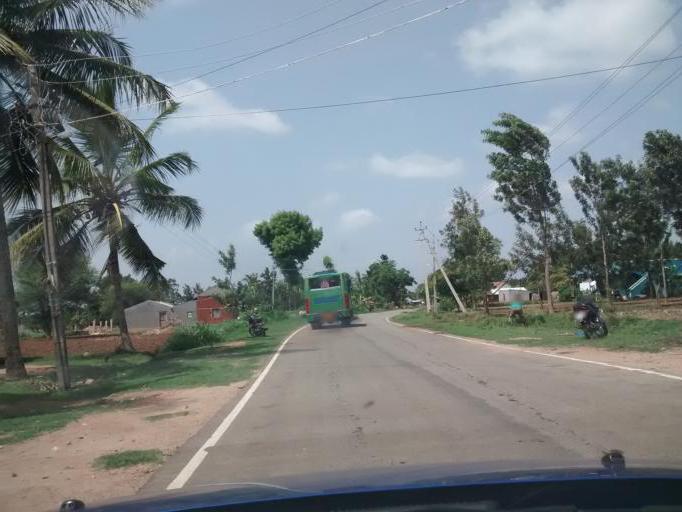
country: IN
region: Karnataka
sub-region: Hassan
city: Hole Narsipur
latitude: 12.6716
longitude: 76.1866
